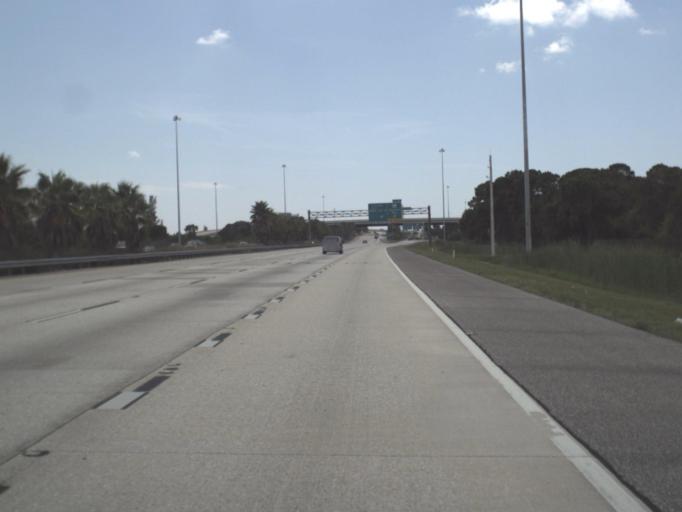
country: US
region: Florida
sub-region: Pinellas County
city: Feather Sound
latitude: 27.8846
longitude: -82.6538
